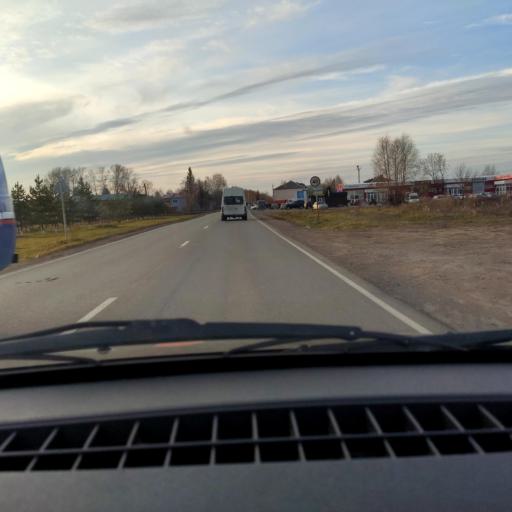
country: RU
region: Bashkortostan
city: Mikhaylovka
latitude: 54.8094
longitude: 55.8134
